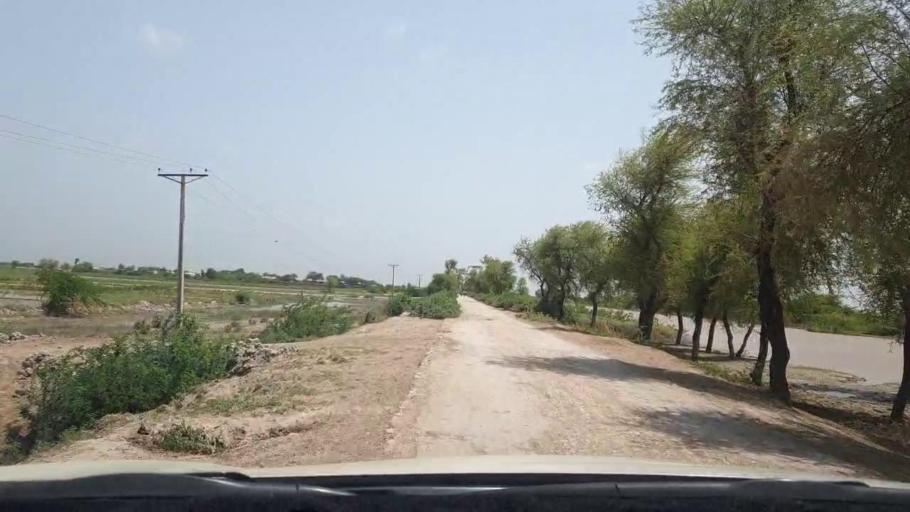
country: PK
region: Sindh
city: Talhar
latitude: 24.9151
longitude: 68.8386
